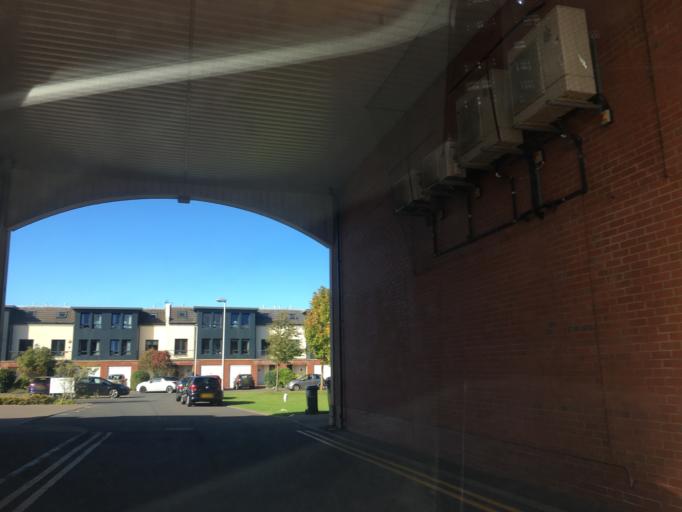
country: GB
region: Scotland
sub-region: Edinburgh
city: Colinton
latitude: 55.9267
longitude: -3.2503
